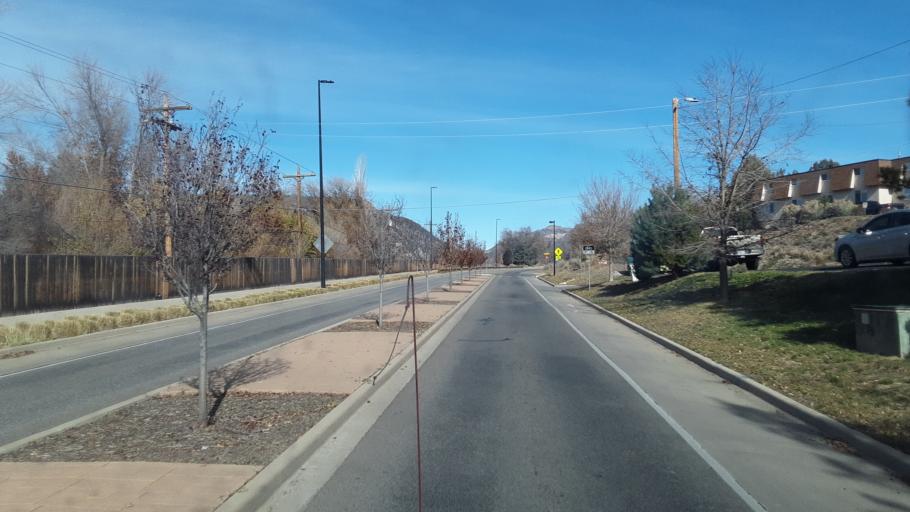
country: US
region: Colorado
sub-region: La Plata County
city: Durango
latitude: 37.2859
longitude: -107.8669
